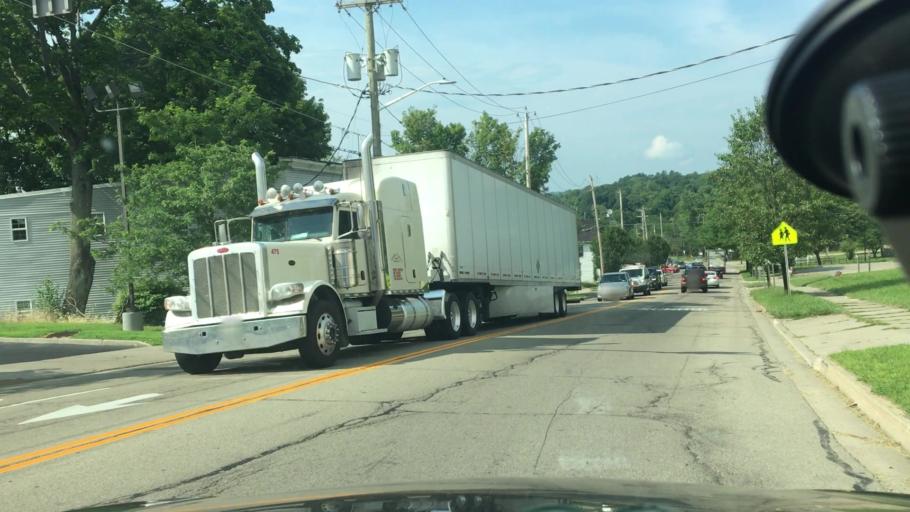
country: US
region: New York
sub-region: Chautauqua County
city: Jamestown
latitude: 42.0991
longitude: -79.2420
